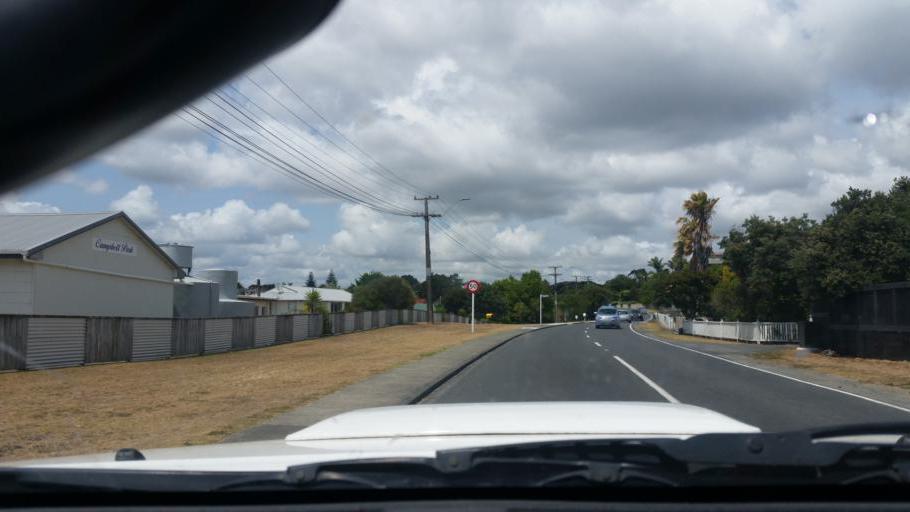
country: NZ
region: Auckland
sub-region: Auckland
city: Wellsford
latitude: -36.0913
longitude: 174.5846
